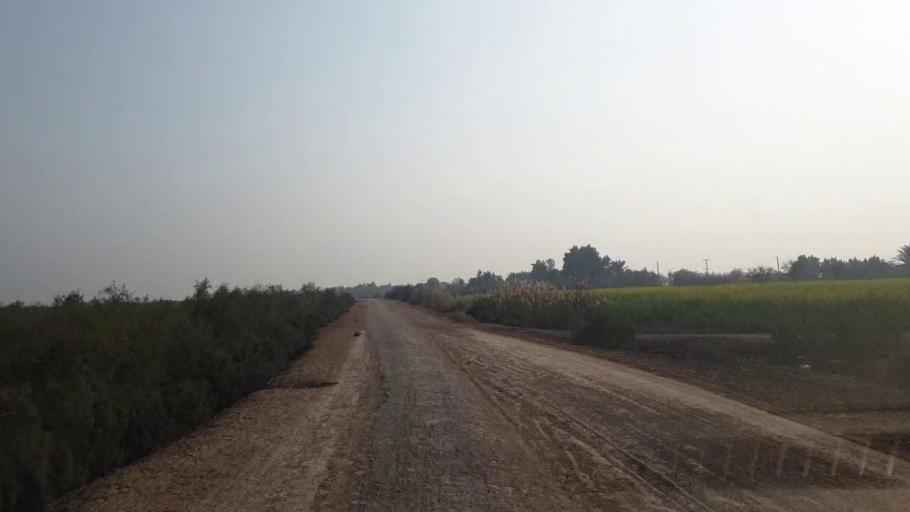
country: PK
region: Sindh
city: Shahdadpur
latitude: 25.9703
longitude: 68.5221
